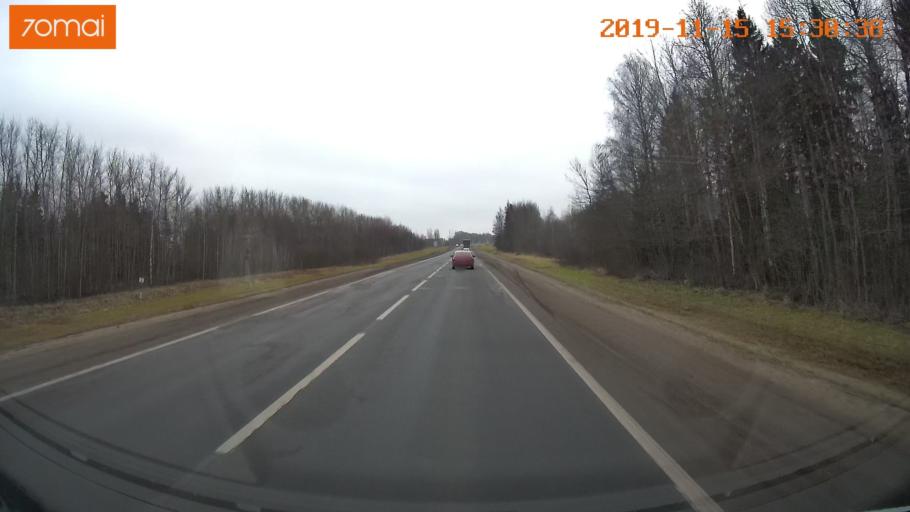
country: RU
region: Jaroslavl
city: Danilov
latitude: 58.1082
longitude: 40.1121
